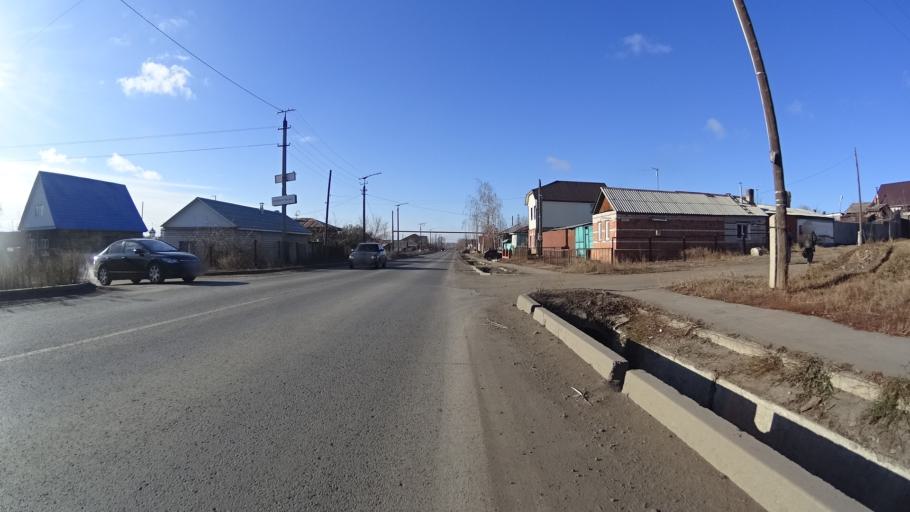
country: RU
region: Chelyabinsk
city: Troitsk
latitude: 54.0970
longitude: 61.5713
